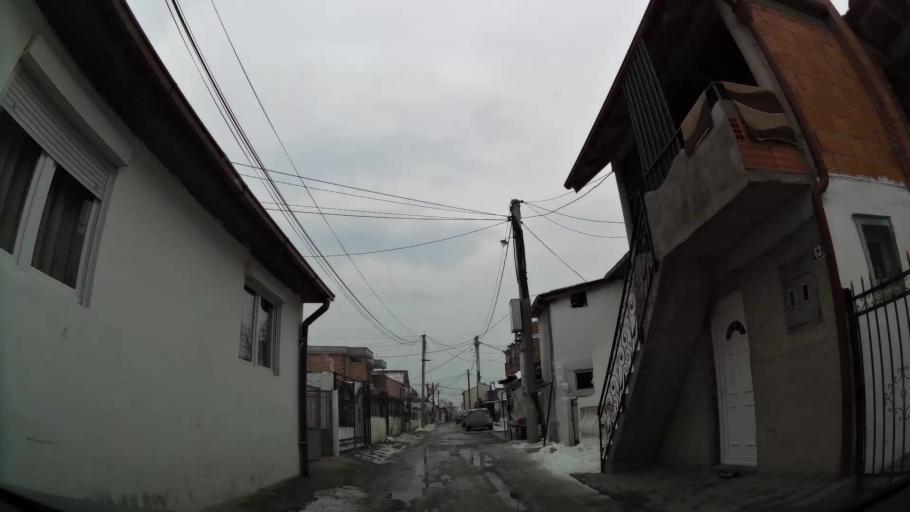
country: MK
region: Suto Orizari
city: Suto Orizare
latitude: 42.0464
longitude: 21.4213
